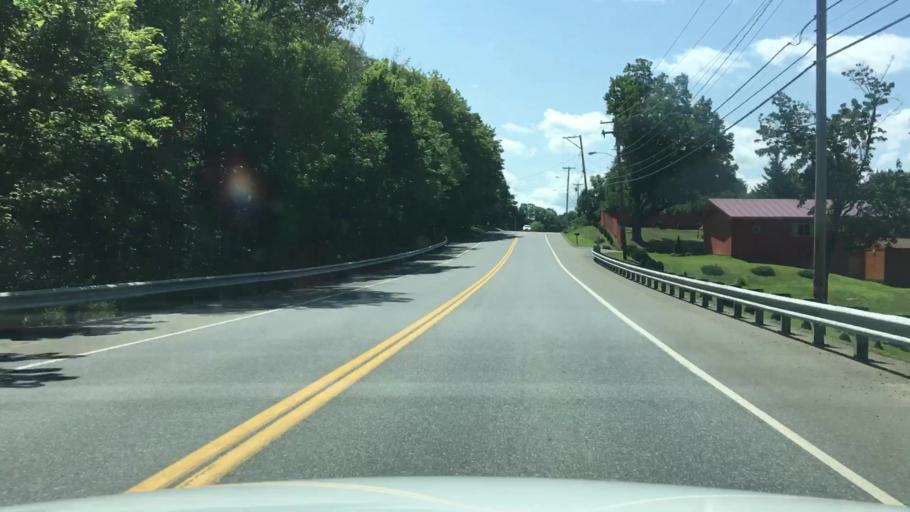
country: US
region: Maine
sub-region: Kennebec County
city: Augusta
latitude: 44.2969
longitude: -69.7678
